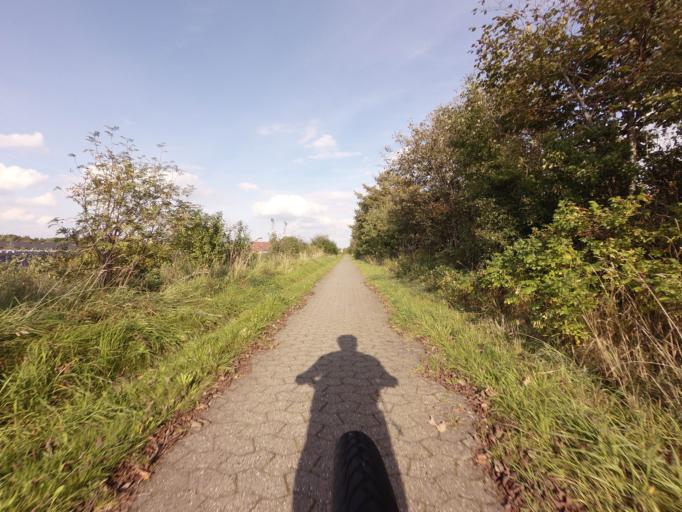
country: DK
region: Central Jutland
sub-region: Viborg Kommune
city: Karup
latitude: 56.3370
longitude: 9.2460
